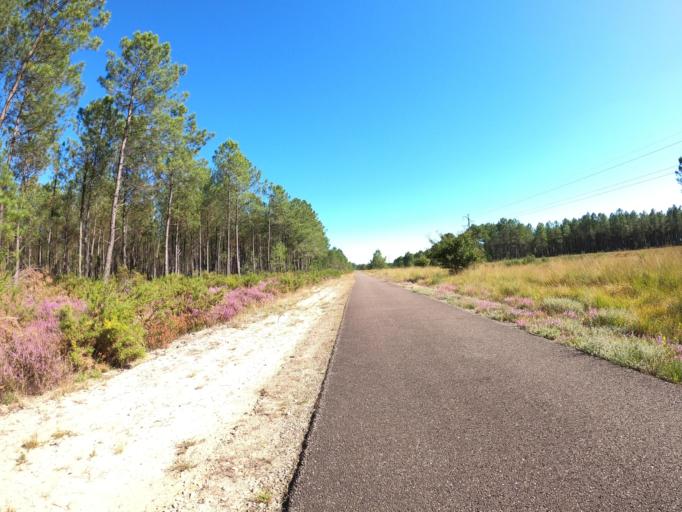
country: FR
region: Aquitaine
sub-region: Departement des Landes
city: Ychoux
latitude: 44.3393
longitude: -0.9622
